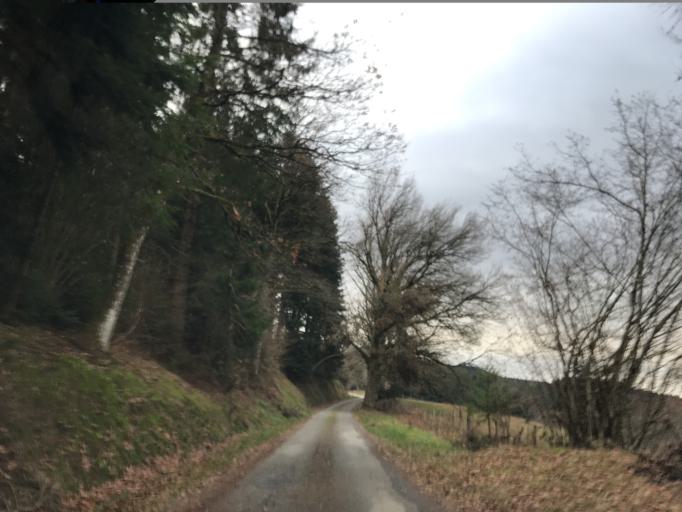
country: FR
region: Auvergne
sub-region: Departement du Puy-de-Dome
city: Celles-sur-Durolle
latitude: 45.8420
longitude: 3.6630
